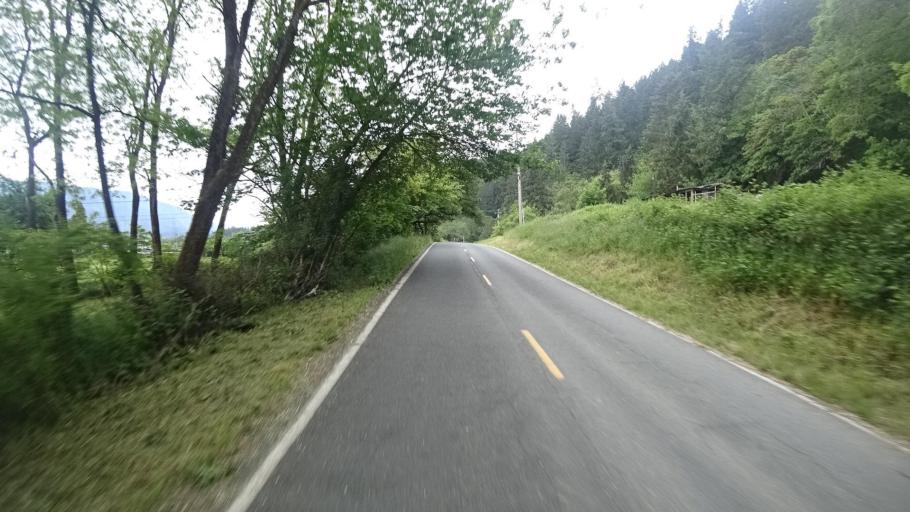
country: US
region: California
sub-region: Humboldt County
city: Willow Creek
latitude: 41.0919
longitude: -123.7133
